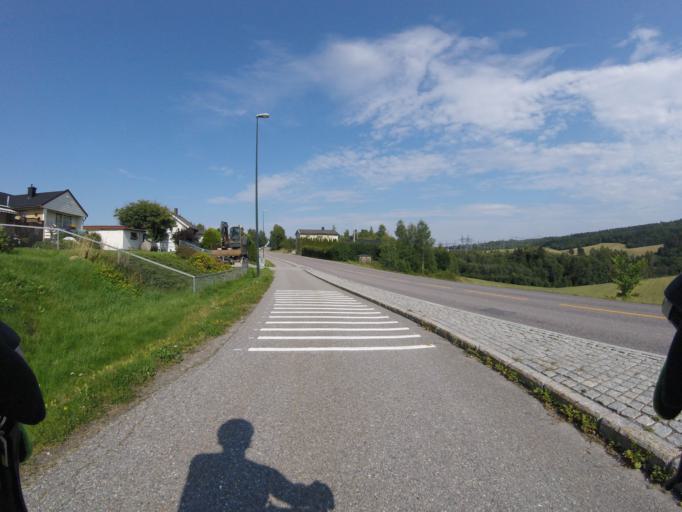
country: NO
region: Akershus
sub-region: Skedsmo
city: Leirsund
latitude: 60.0032
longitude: 11.1014
